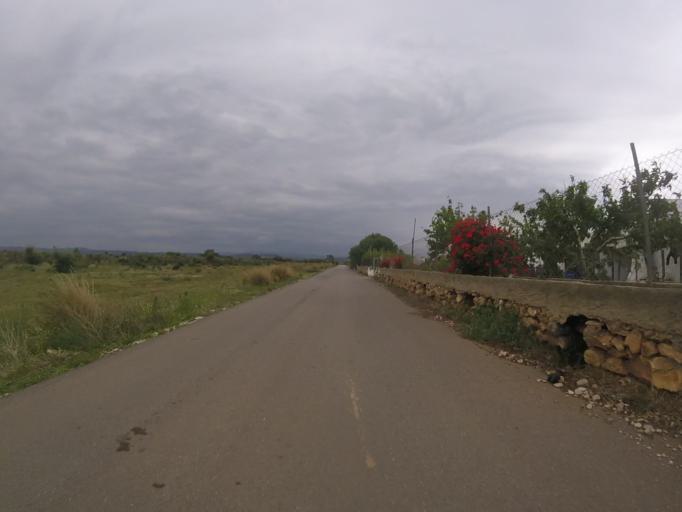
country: ES
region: Valencia
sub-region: Provincia de Castello
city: Torreblanca
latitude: 40.2130
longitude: 0.2480
